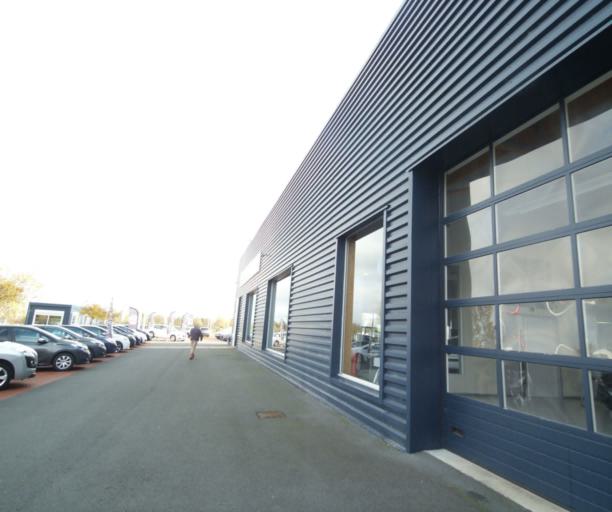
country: FR
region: Poitou-Charentes
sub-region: Departement de la Charente-Maritime
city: Saint-Georges-des-Coteaux
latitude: 45.7538
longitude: -0.6783
